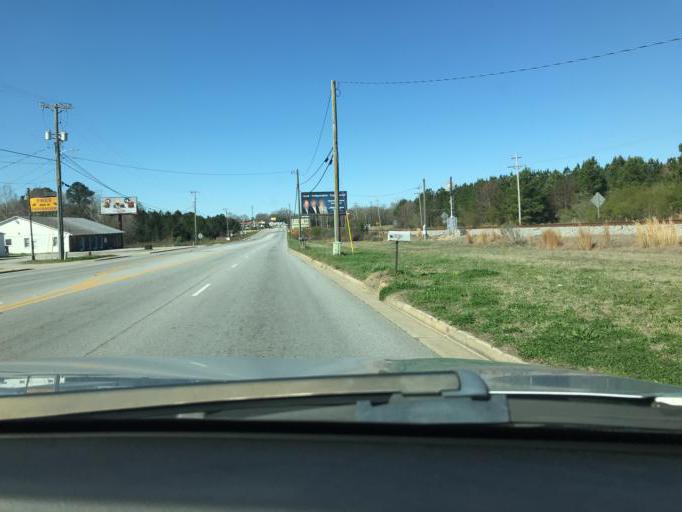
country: US
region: South Carolina
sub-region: Laurens County
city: Clinton
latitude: 34.4709
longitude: -81.8980
